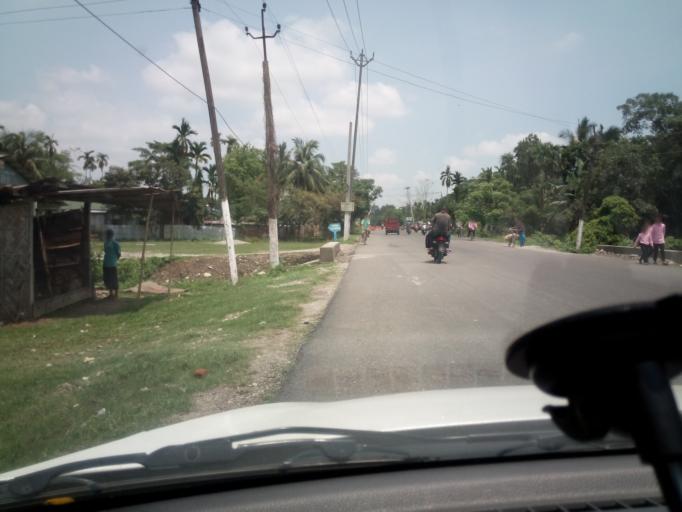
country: IN
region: Assam
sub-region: Udalguri
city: Udalguri
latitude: 26.7106
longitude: 92.2086
